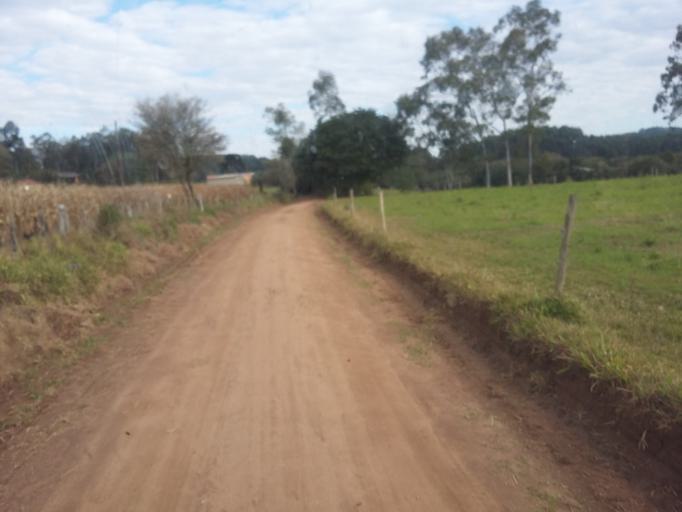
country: BR
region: Rio Grande do Sul
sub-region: Camaqua
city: Camaqua
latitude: -30.7136
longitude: -51.7838
